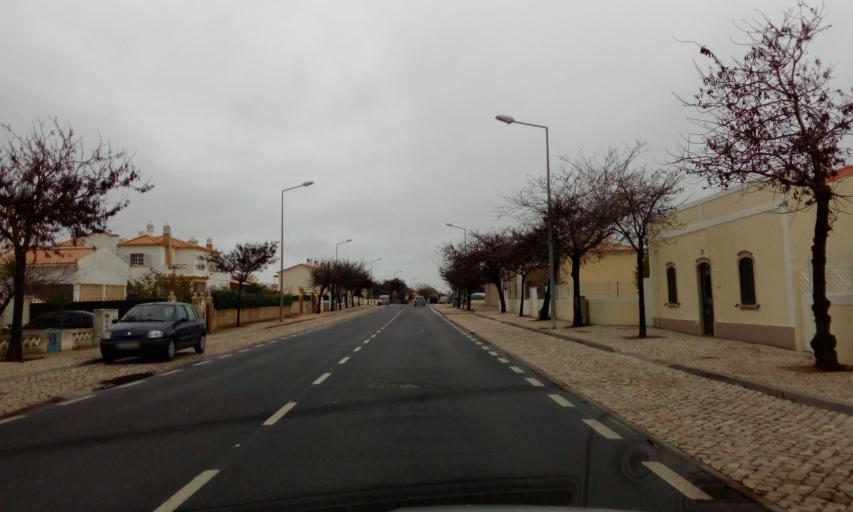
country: PT
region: Faro
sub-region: Albufeira
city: Ferreiras
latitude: 37.1248
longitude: -8.2286
